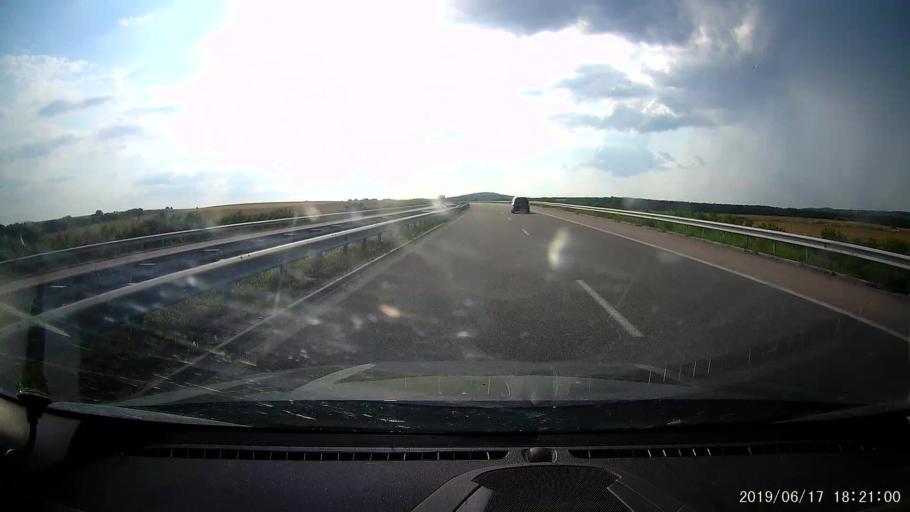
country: BG
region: Khaskovo
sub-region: Obshtina Simeonovgrad
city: Simeonovgrad
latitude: 41.9659
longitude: 25.7965
